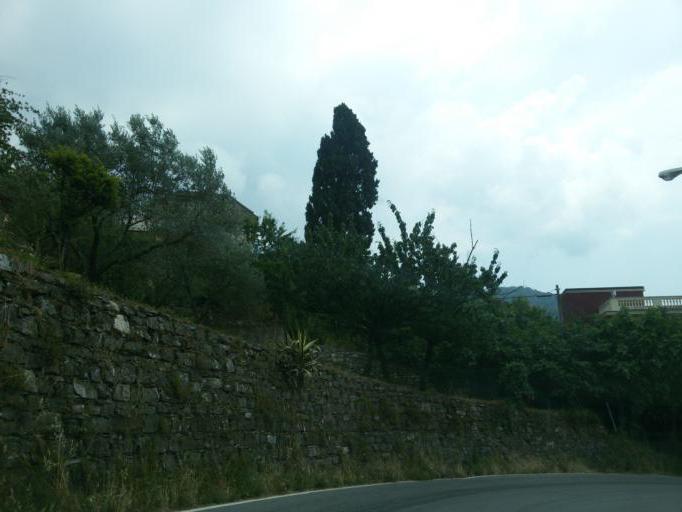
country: IT
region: Liguria
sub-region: Provincia di Genova
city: Bogliasco
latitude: 44.4330
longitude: 9.0213
